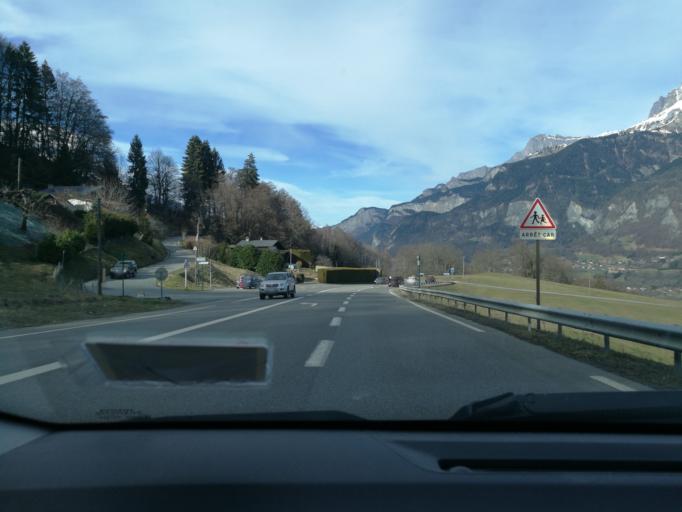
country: FR
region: Rhone-Alpes
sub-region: Departement de la Haute-Savoie
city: Domancy
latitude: 45.9135
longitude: 6.6358
